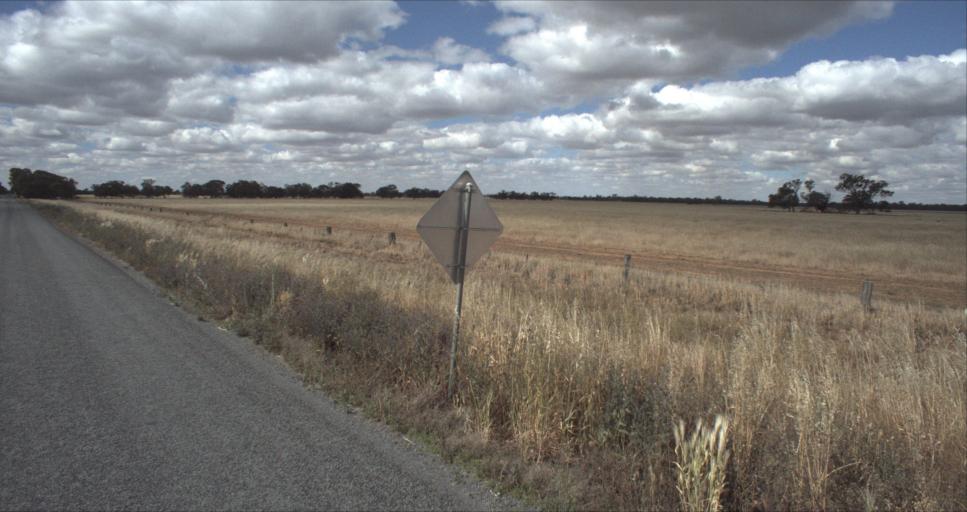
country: AU
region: New South Wales
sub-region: Leeton
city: Leeton
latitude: -34.6957
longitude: 146.3429
